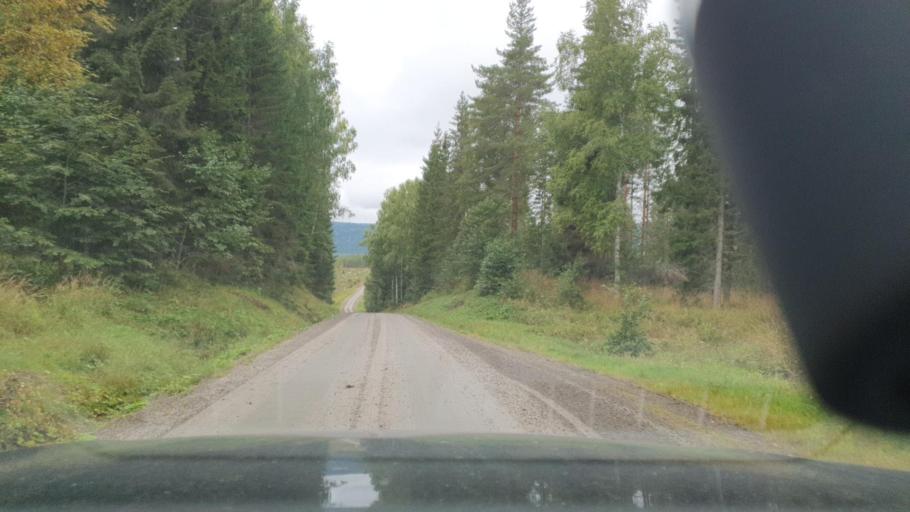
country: SE
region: Vaermland
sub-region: Torsby Kommun
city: Torsby
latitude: 60.4453
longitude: 12.9143
